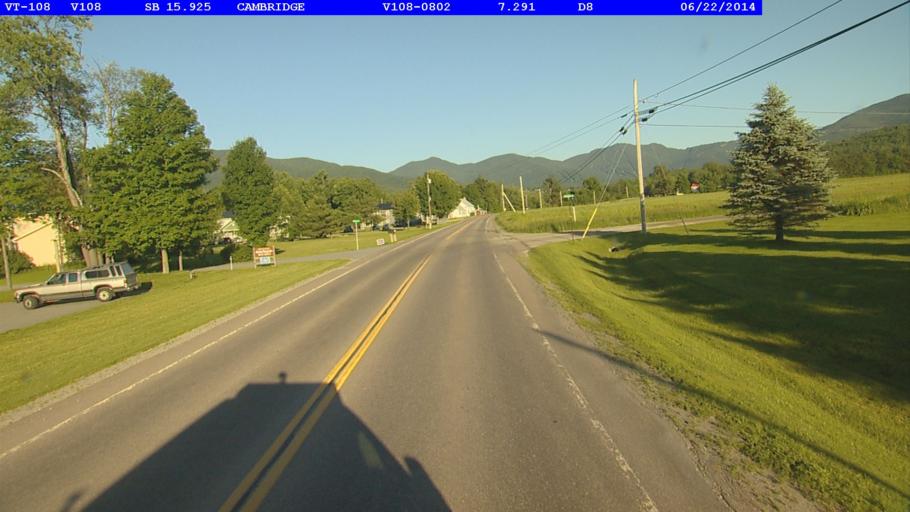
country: US
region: Vermont
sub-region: Lamoille County
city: Johnson
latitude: 44.6249
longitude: -72.8278
